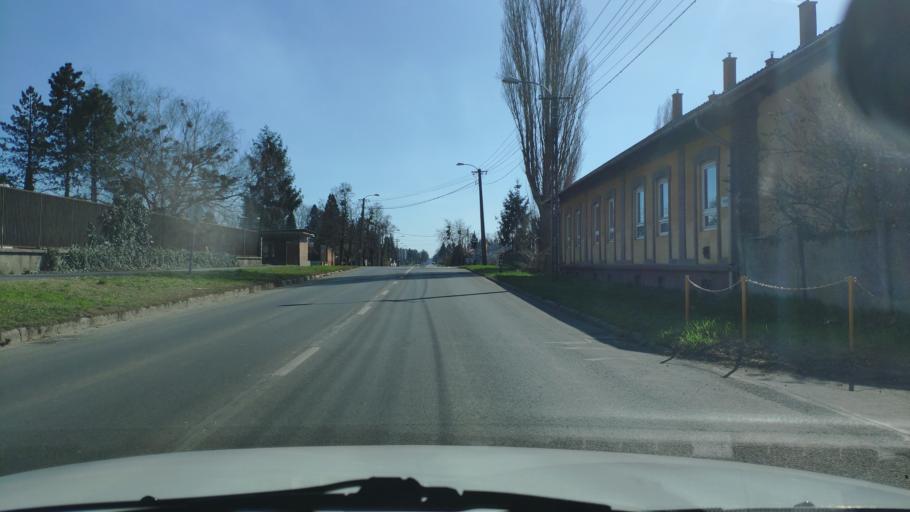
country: HU
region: Zala
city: Nagykanizsa
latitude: 46.4360
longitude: 16.9882
